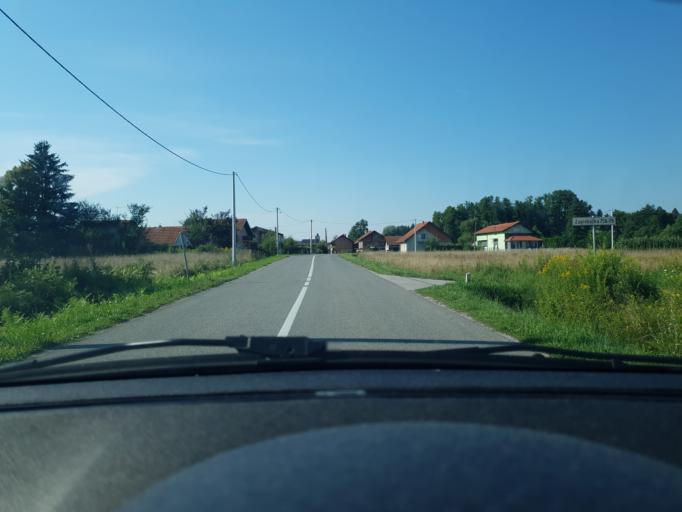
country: HR
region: Zagrebacka
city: Jakovlje
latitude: 45.9308
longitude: 15.8452
